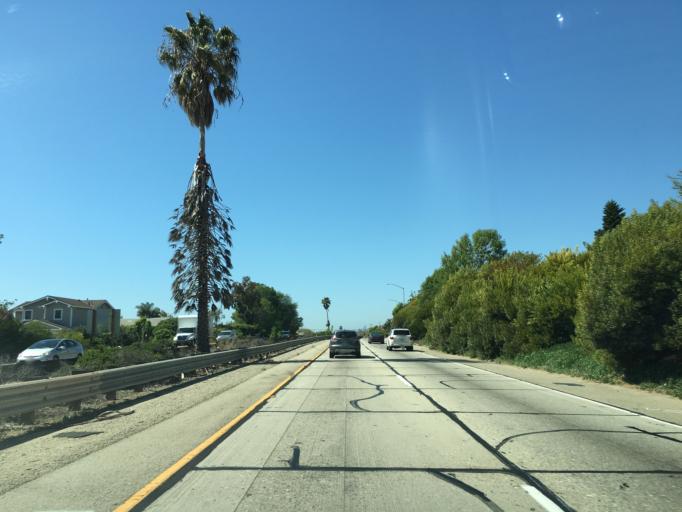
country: US
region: California
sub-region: Santa Barbara County
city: Carpinteria
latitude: 34.4035
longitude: -119.5272
